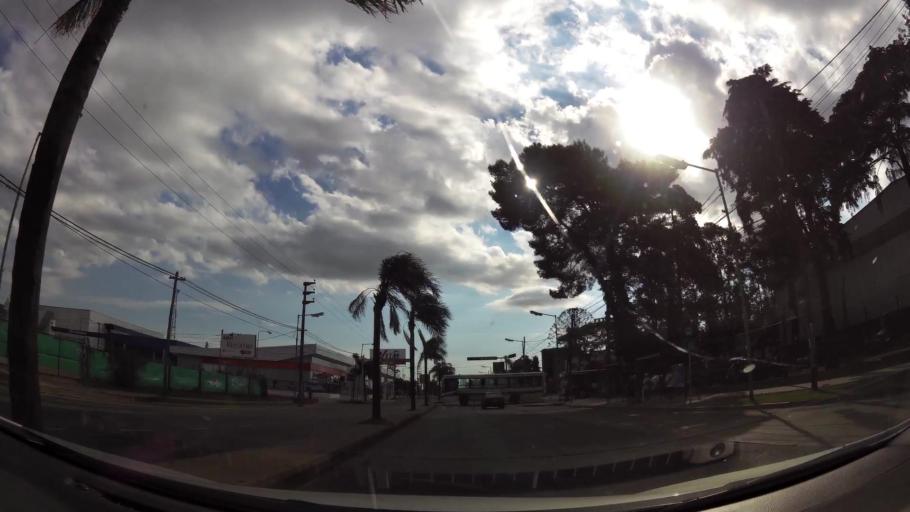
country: AR
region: Buenos Aires
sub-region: Partido de Tigre
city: Tigre
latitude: -34.4727
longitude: -58.6574
